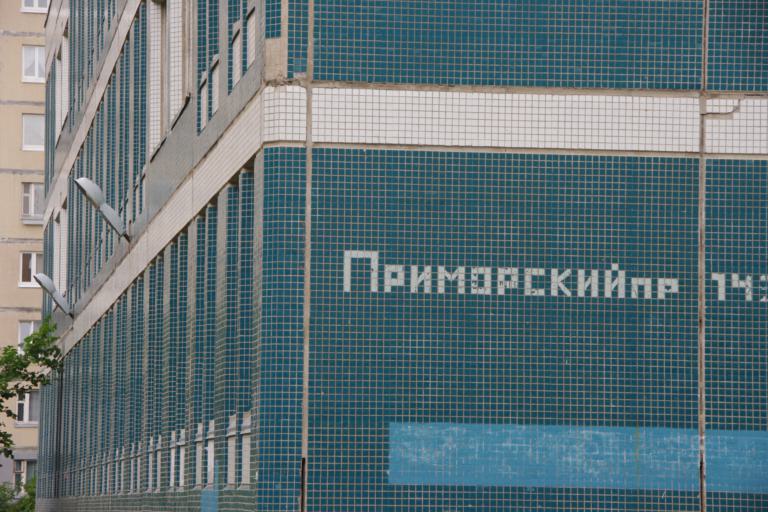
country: RU
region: Leningrad
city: Untolovo
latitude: 59.9854
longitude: 30.2086
